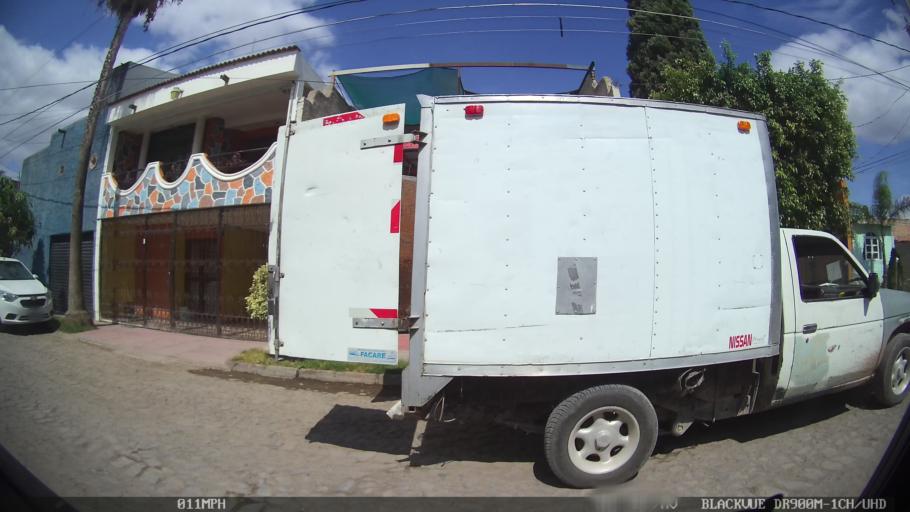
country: MX
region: Jalisco
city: Tonala
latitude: 20.6683
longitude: -103.2375
